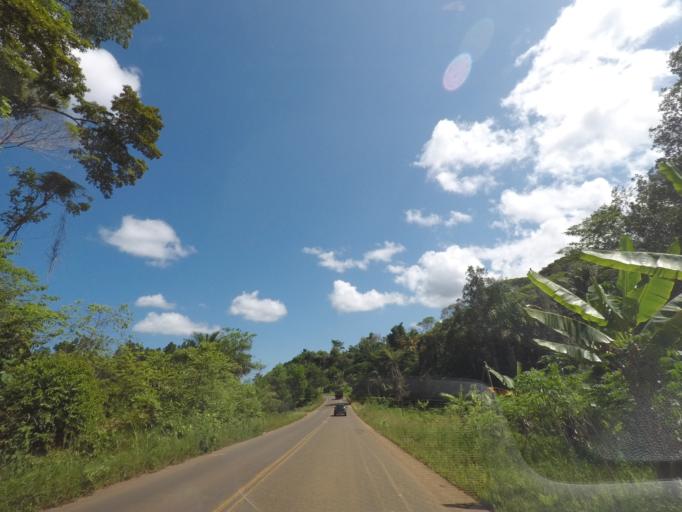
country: BR
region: Bahia
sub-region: Taperoa
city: Taperoa
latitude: -13.5947
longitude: -39.1072
